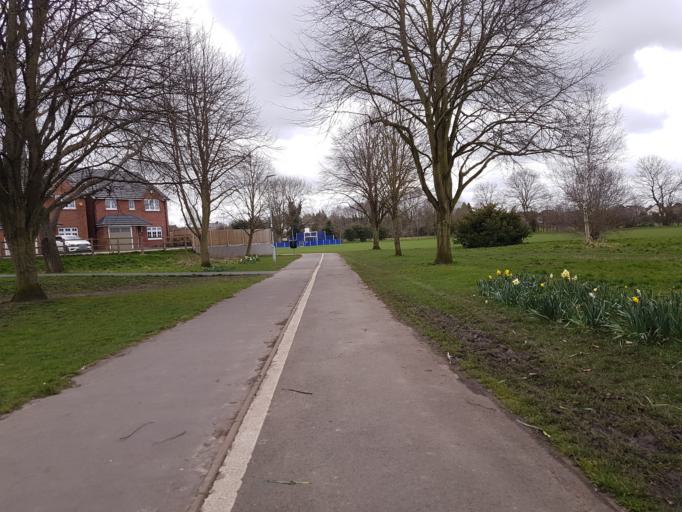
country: GB
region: England
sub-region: Leicestershire
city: Hinckley
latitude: 52.5403
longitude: -1.3846
